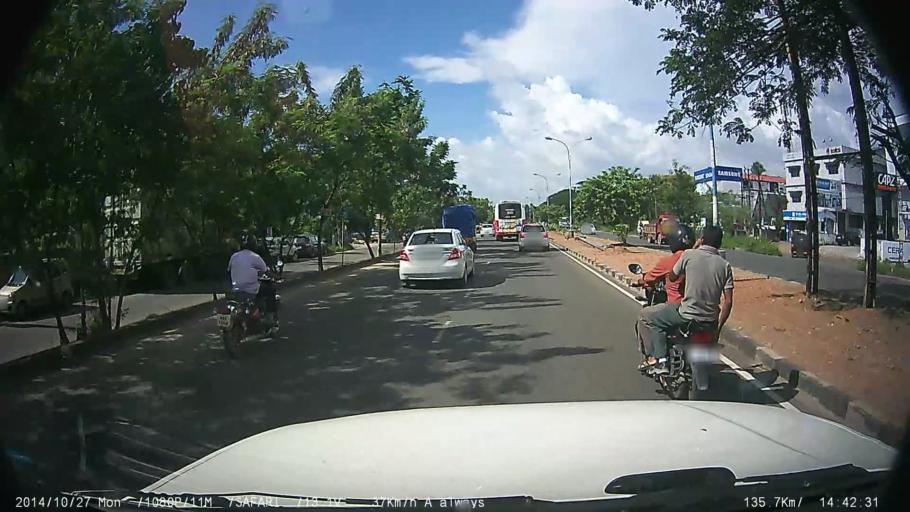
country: IN
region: Kerala
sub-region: Ernakulam
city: Elur
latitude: 10.0110
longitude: 76.3120
